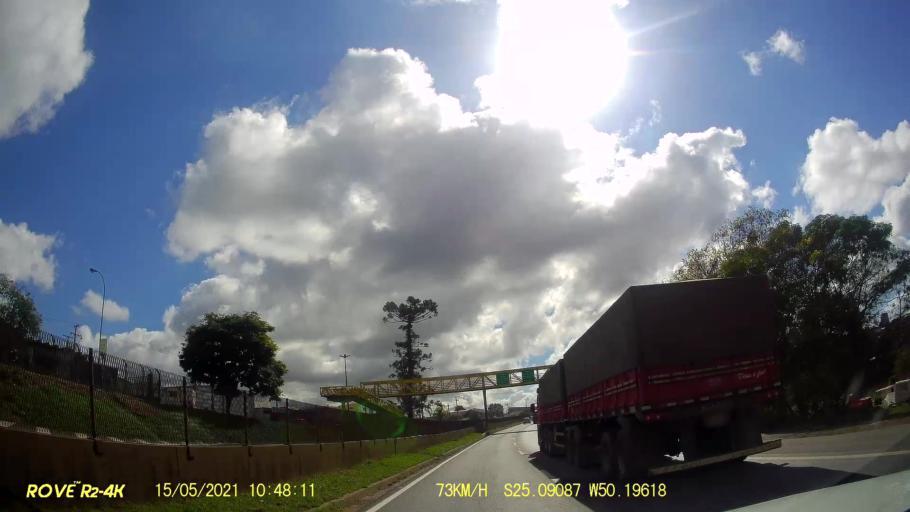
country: BR
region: Parana
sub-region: Ponta Grossa
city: Ponta Grossa
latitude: -25.0909
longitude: -50.1962
